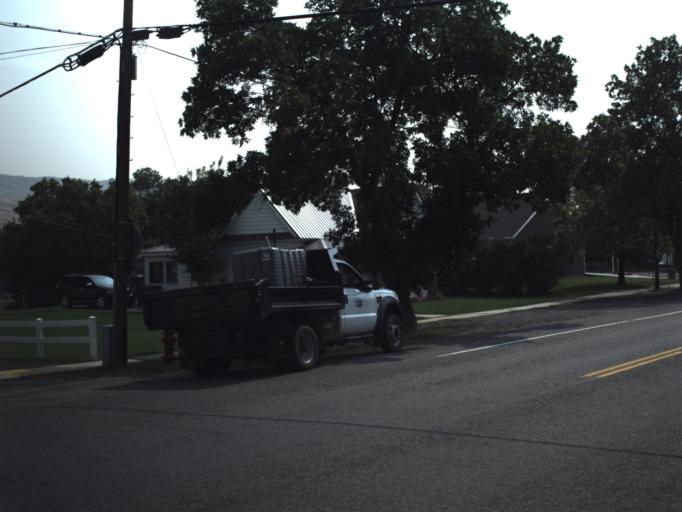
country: US
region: Utah
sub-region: Summit County
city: Coalville
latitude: 41.0170
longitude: -111.4985
